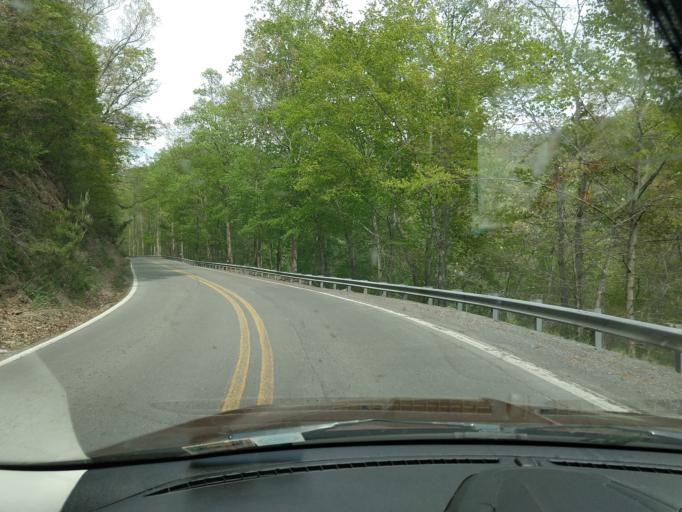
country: US
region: West Virginia
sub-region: McDowell County
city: Welch
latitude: 37.3615
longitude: -81.6441
